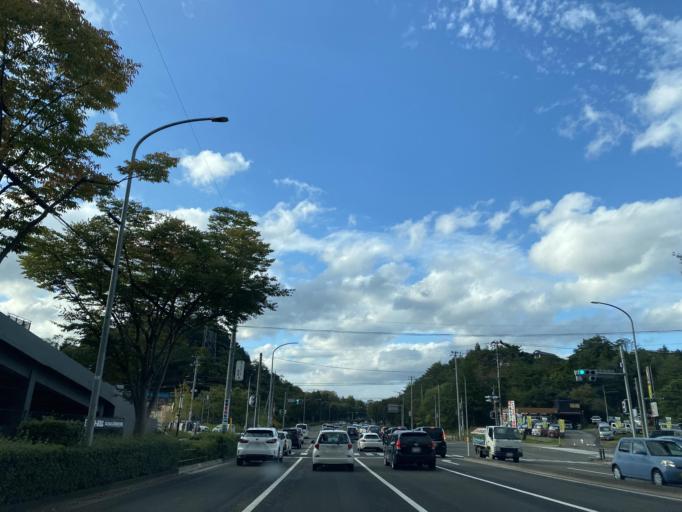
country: JP
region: Miyagi
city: Sendai-shi
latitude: 38.3101
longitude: 140.8481
